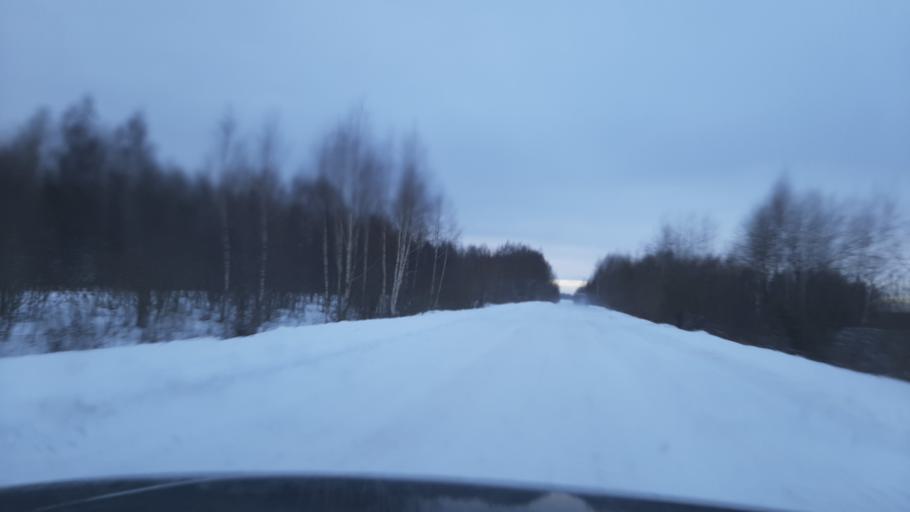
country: RU
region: Kostroma
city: Volgorechensk
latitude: 57.4489
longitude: 41.0158
